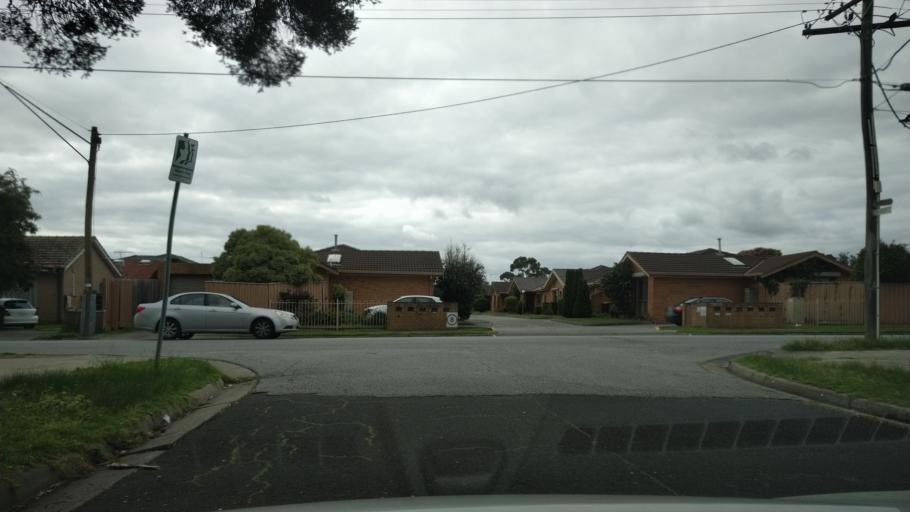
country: AU
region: Victoria
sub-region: Greater Dandenong
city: Springvale South
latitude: -37.9722
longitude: 145.1566
